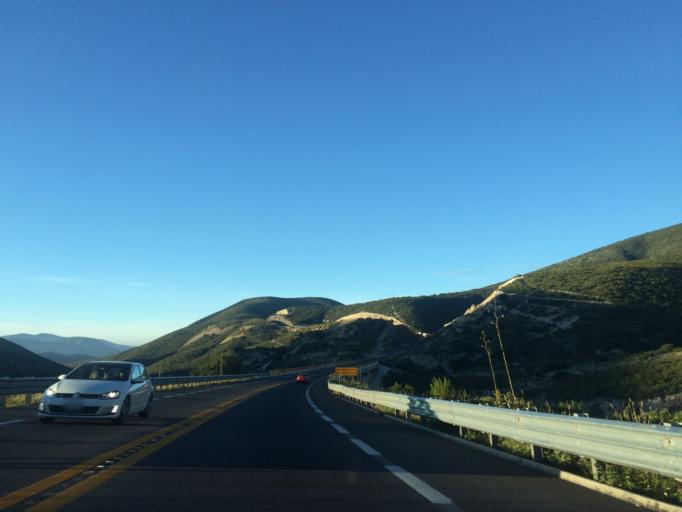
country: MX
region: Puebla
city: Chapuco
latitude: 18.6675
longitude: -97.4566
